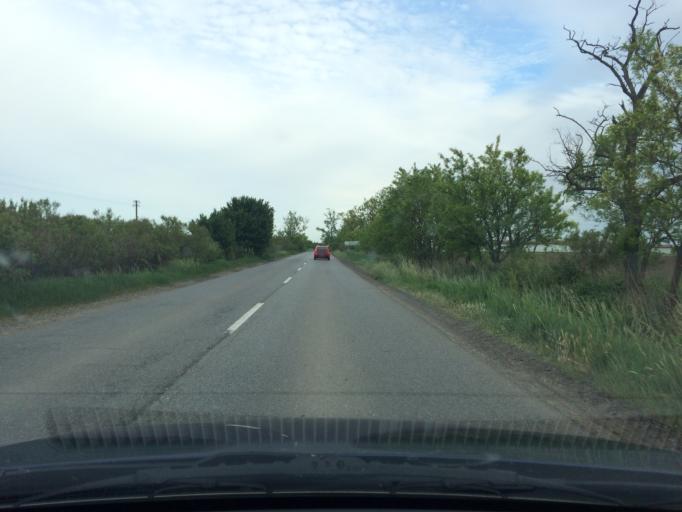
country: HU
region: Szabolcs-Szatmar-Bereg
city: Tiszavasvari
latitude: 47.9260
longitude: 21.3886
